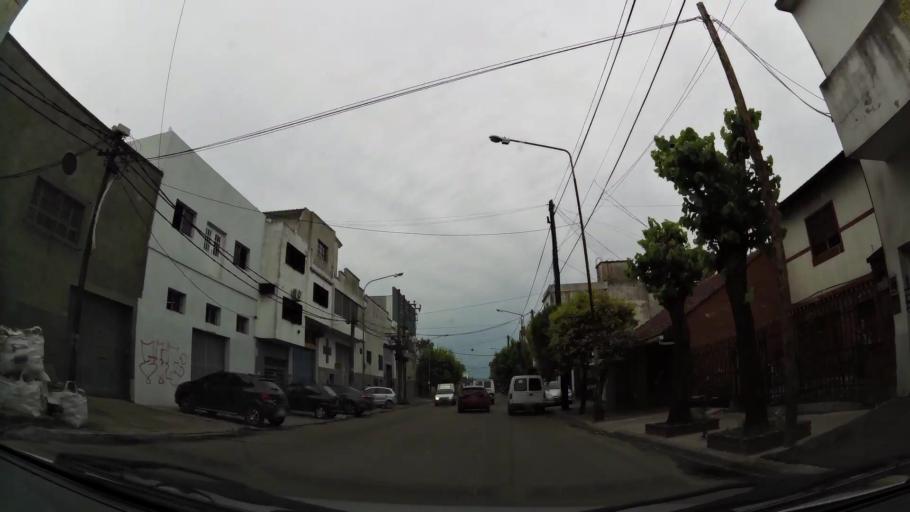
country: AR
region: Buenos Aires
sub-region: Partido de Lanus
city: Lanus
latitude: -34.7000
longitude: -58.3731
